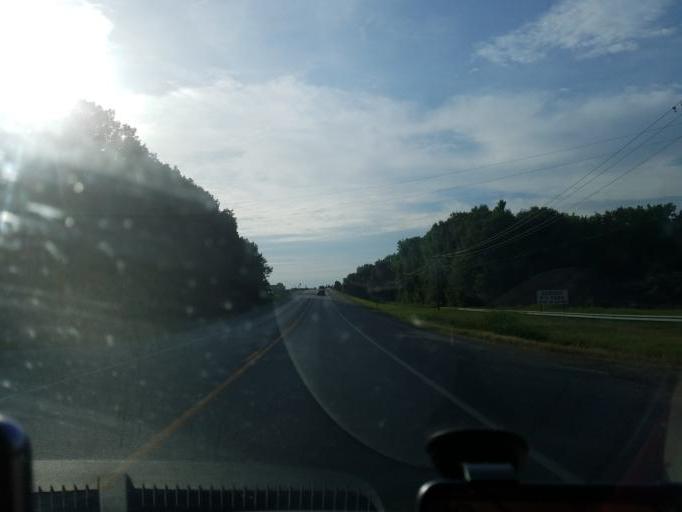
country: US
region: Arkansas
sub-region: White County
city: Bald Knob
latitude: 35.3112
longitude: -91.5601
